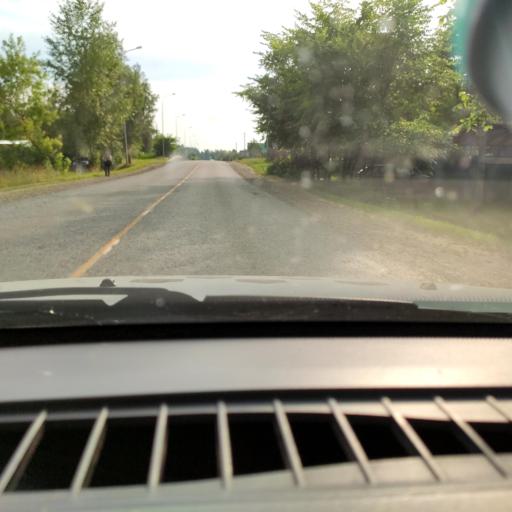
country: RU
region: Udmurtiya
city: Igra
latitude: 57.5752
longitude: 53.1399
